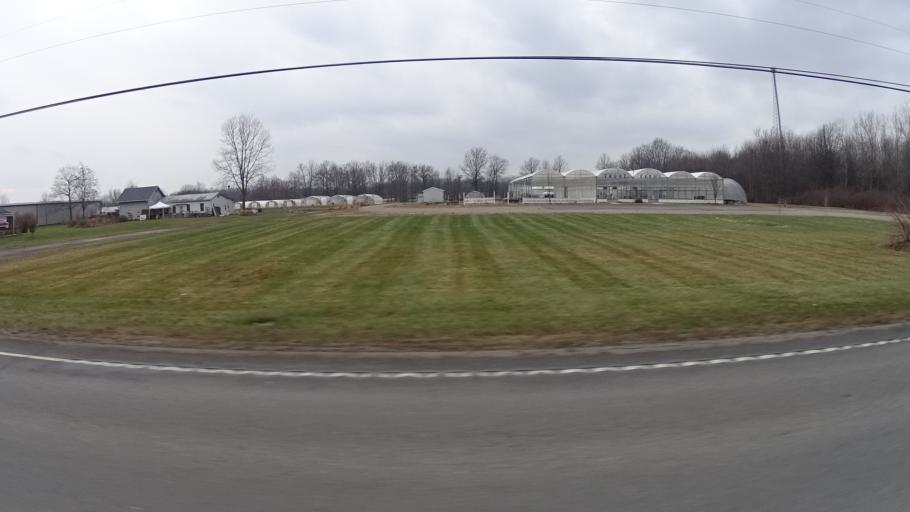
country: US
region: Ohio
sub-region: Lorain County
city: Amherst
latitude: 41.3594
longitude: -82.2105
